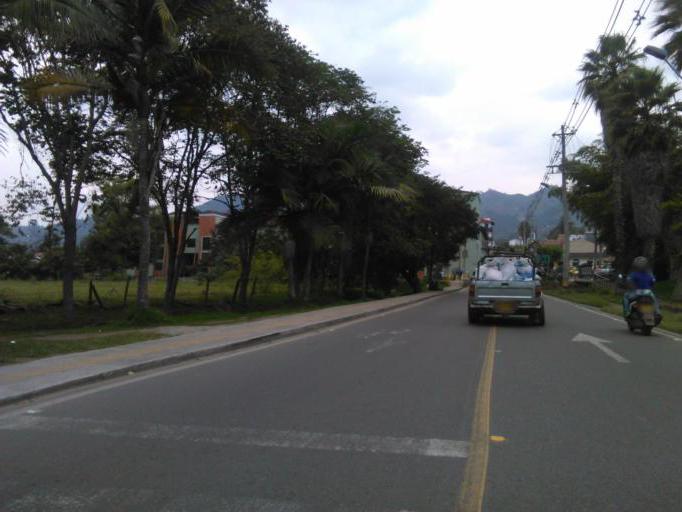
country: CO
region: Antioquia
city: La Ceja
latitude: 6.0292
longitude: -75.4281
